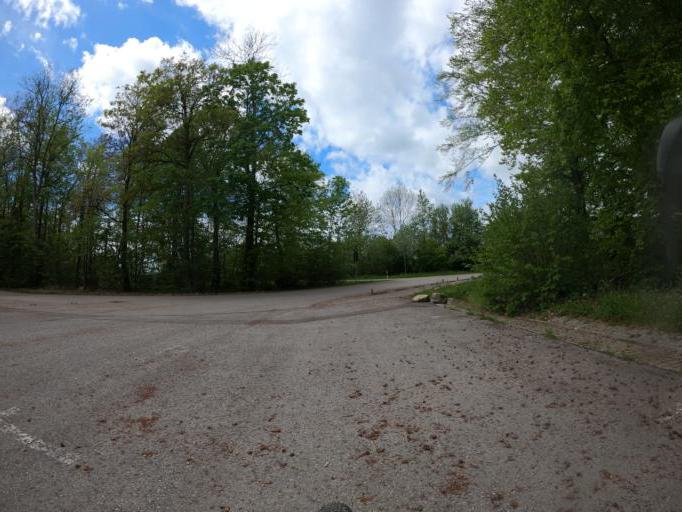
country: DE
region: Baden-Wuerttemberg
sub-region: Regierungsbezirk Stuttgart
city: Oberjettingen
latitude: 48.5698
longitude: 8.7610
